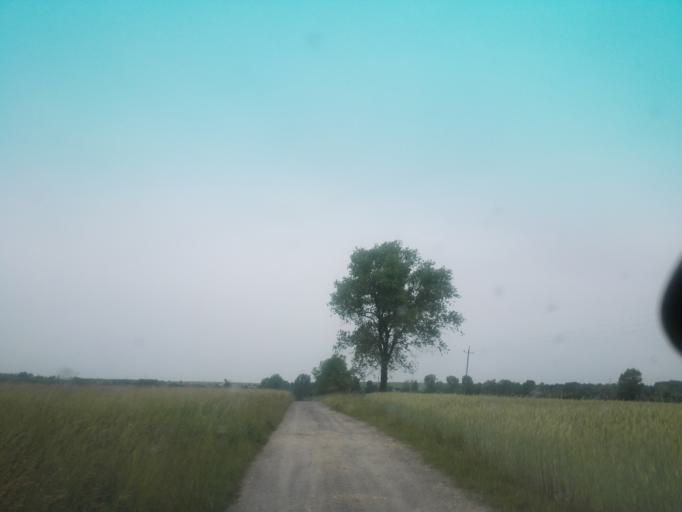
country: PL
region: Silesian Voivodeship
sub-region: Powiat czestochowski
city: Mstow
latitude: 50.7867
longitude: 19.3212
